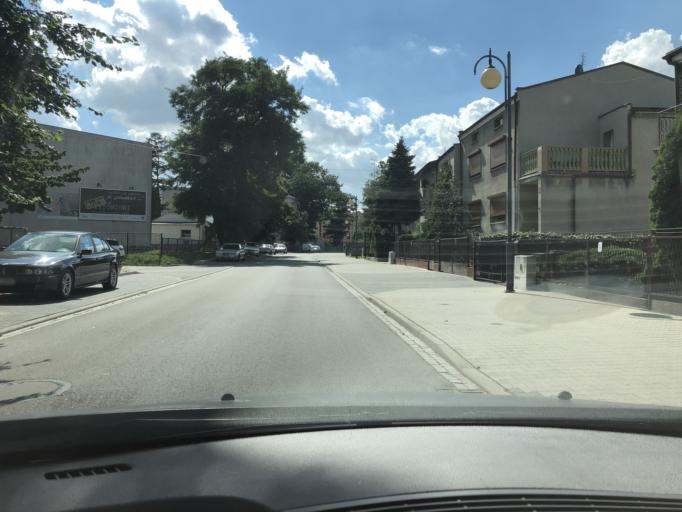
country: PL
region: Lodz Voivodeship
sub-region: Powiat wieruszowski
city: Wieruszow
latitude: 51.2965
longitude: 18.1588
